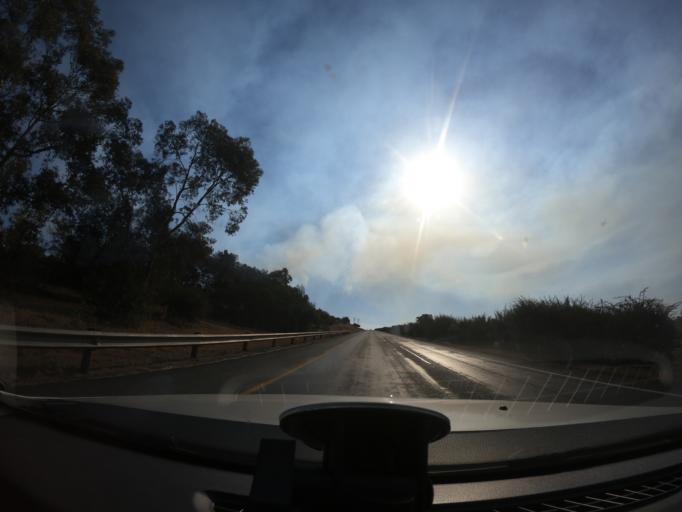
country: ZA
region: Gauteng
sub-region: Sedibeng District Municipality
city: Heidelberg
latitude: -26.4748
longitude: 28.3505
